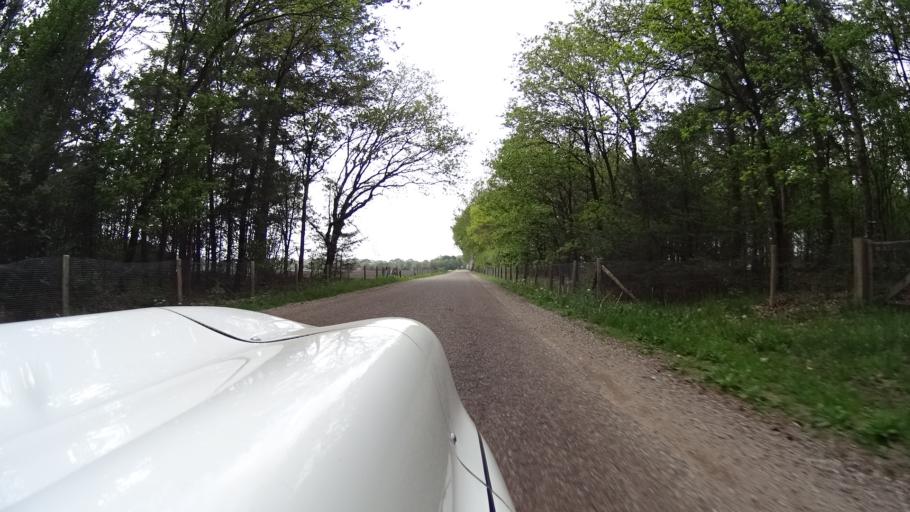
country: NL
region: North Brabant
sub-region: Gemeente Uden
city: Odiliapeel
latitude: 51.6301
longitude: 5.7253
